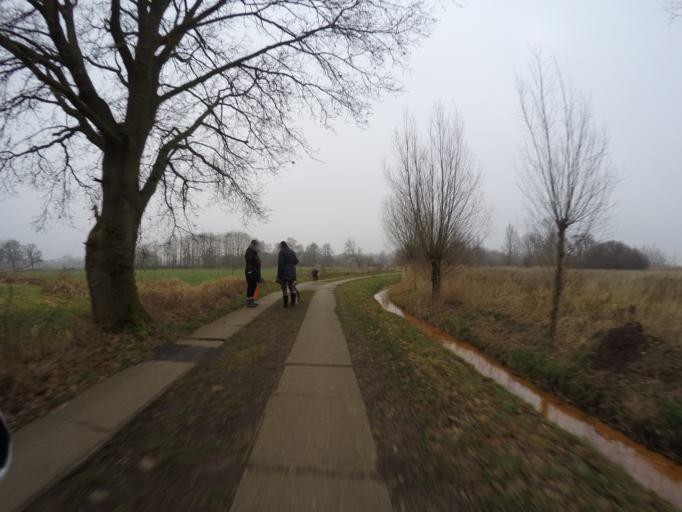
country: DE
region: Schleswig-Holstein
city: Borstel-Hohenraden
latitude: 53.6719
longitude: 9.8199
